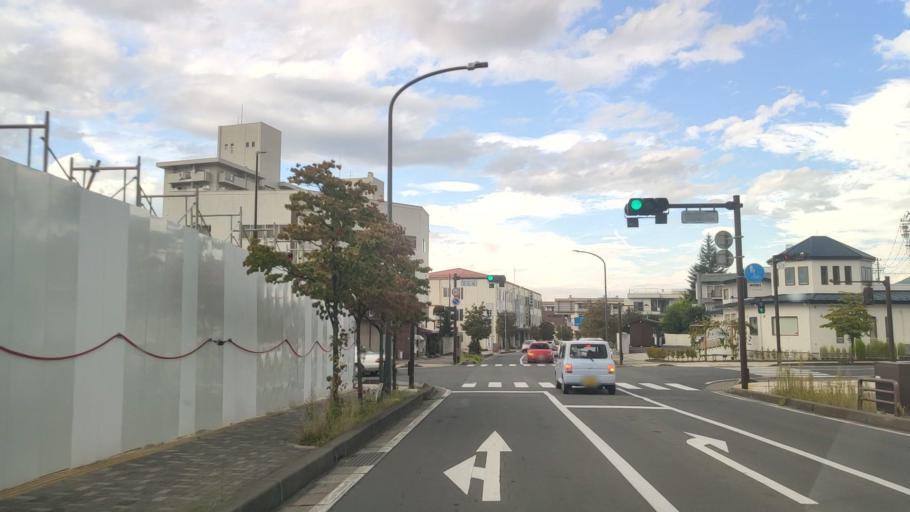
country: JP
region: Nagano
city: Suzaka
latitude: 36.6562
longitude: 138.3076
